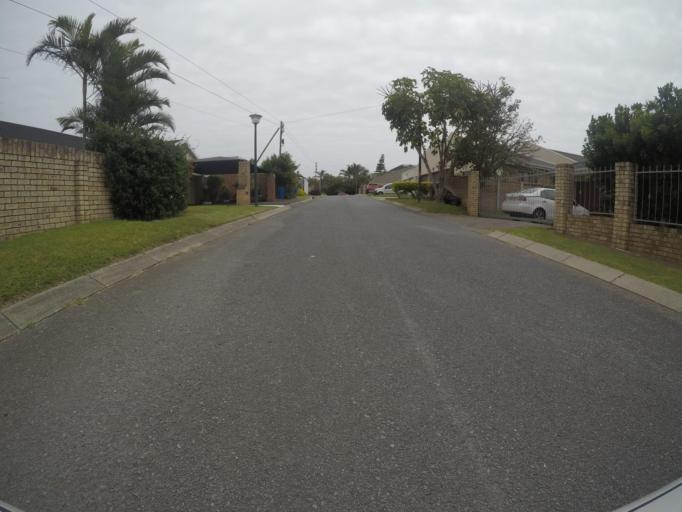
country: ZA
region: Eastern Cape
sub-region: Buffalo City Metropolitan Municipality
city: East London
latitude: -32.9772
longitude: 27.9530
